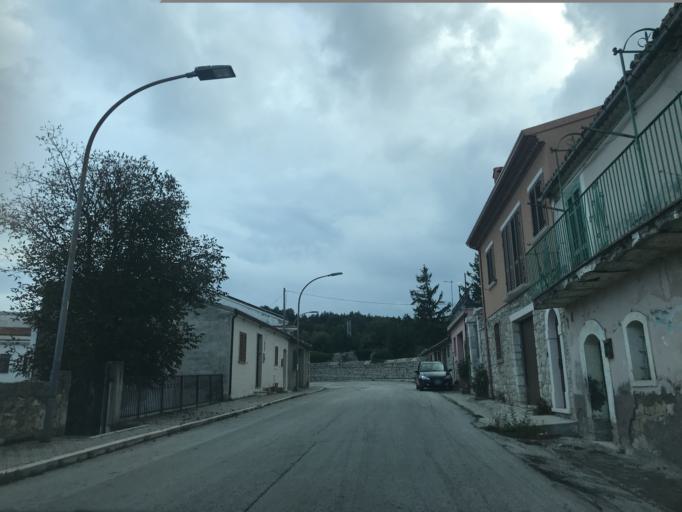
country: IT
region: Molise
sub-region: Provincia di Campobasso
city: Duronia
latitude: 41.6587
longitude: 14.4603
